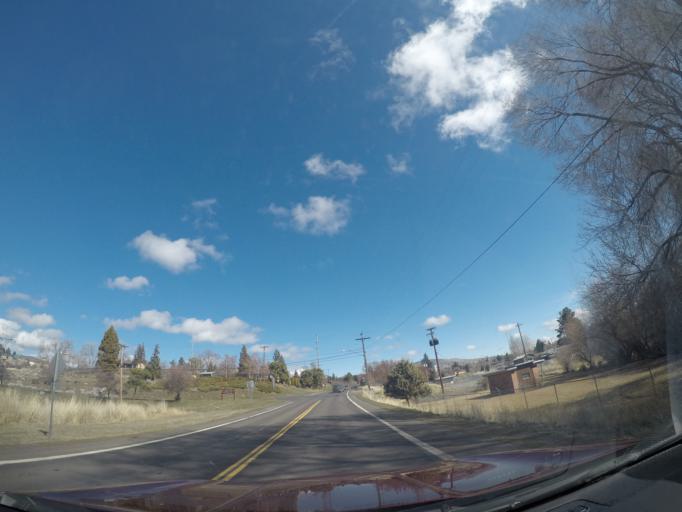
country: US
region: Oregon
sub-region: Klamath County
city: Klamath Falls
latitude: 42.2391
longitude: -121.8045
